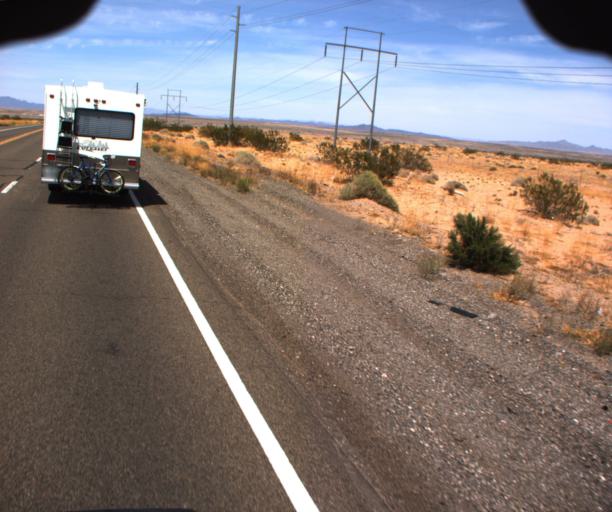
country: US
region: Arizona
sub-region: La Paz County
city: Parker
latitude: 33.9556
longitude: -114.2169
